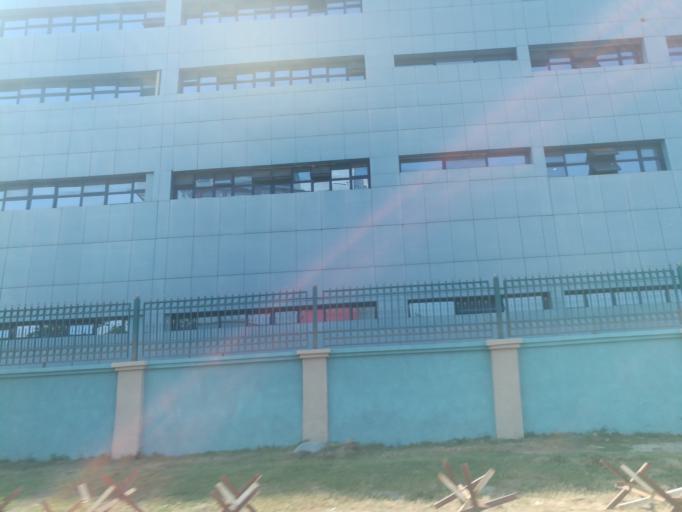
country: NG
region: Abuja Federal Capital Territory
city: Abuja
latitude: 9.0708
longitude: 7.4350
